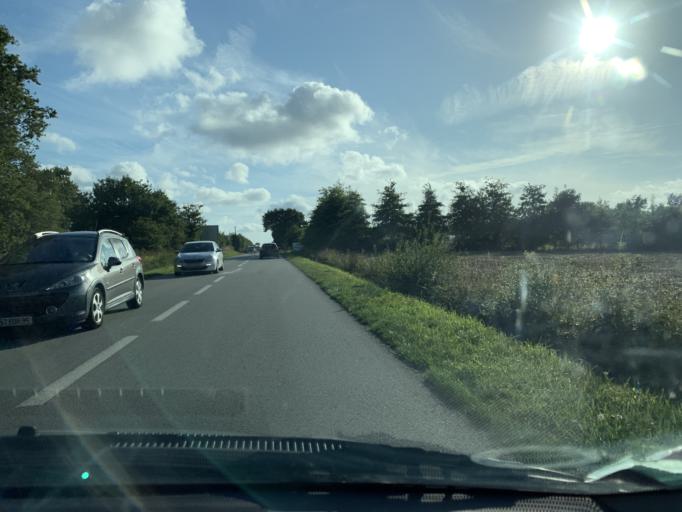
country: FR
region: Brittany
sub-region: Departement du Morbihan
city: Sarzeau
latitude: 47.5552
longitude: -2.7029
